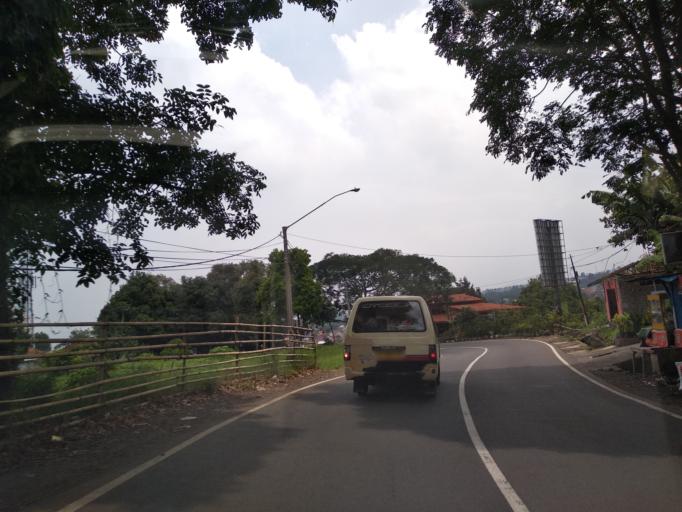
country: ID
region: West Java
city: Lembang
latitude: -6.8361
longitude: 107.6004
